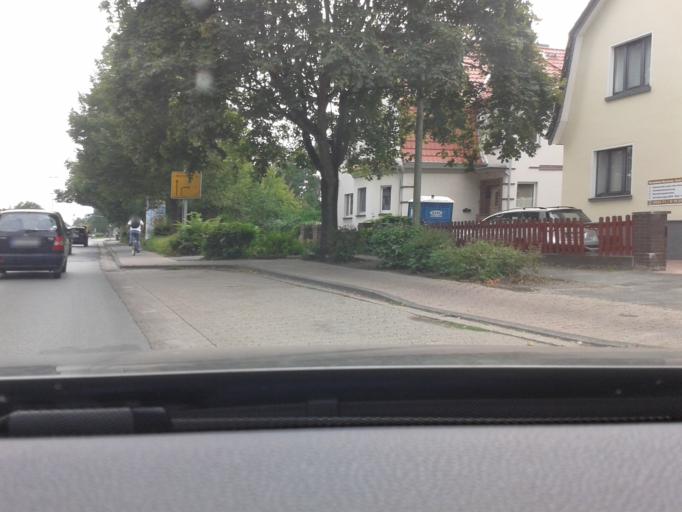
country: DE
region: Lower Saxony
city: Gifhorn
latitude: 52.4709
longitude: 10.5430
